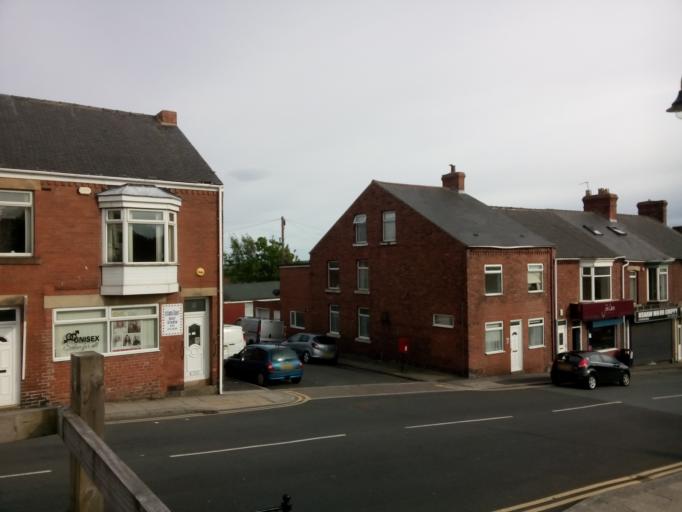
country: GB
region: England
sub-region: County Durham
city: Ushaw Moor
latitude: 54.7777
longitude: -1.6461
